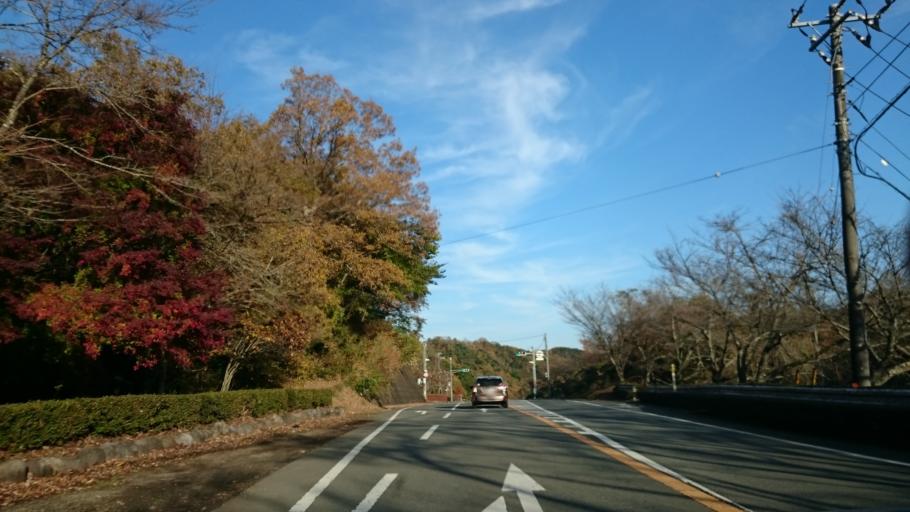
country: JP
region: Shizuoka
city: Heda
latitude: 34.9768
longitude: 138.9175
